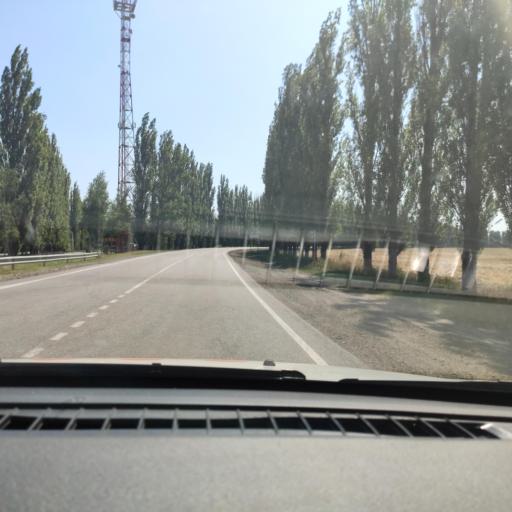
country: RU
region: Voronezj
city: Imeni Pervogo Maya
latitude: 50.7235
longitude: 39.4070
